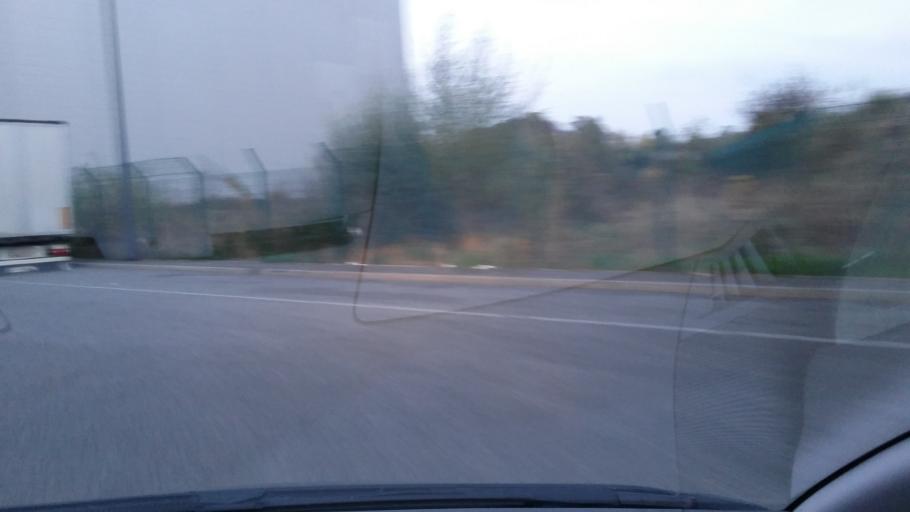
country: FR
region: Alsace
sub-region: Departement du Bas-Rhin
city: Drulingen
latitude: 48.8664
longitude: 7.2762
